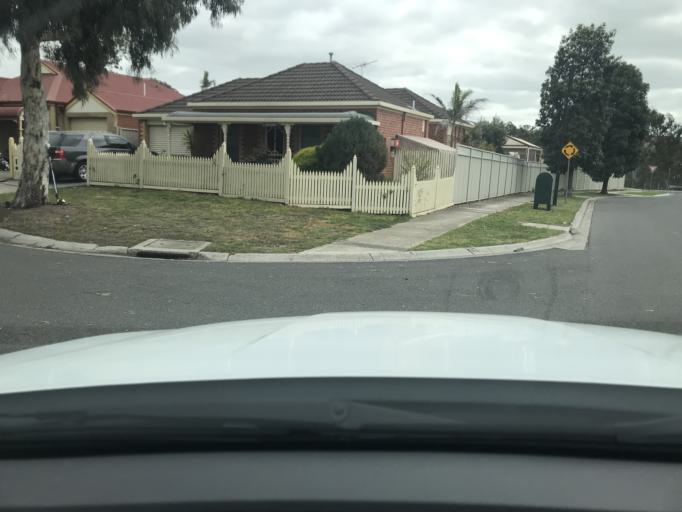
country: AU
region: Victoria
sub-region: Hume
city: Craigieburn
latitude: -37.5877
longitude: 144.9297
